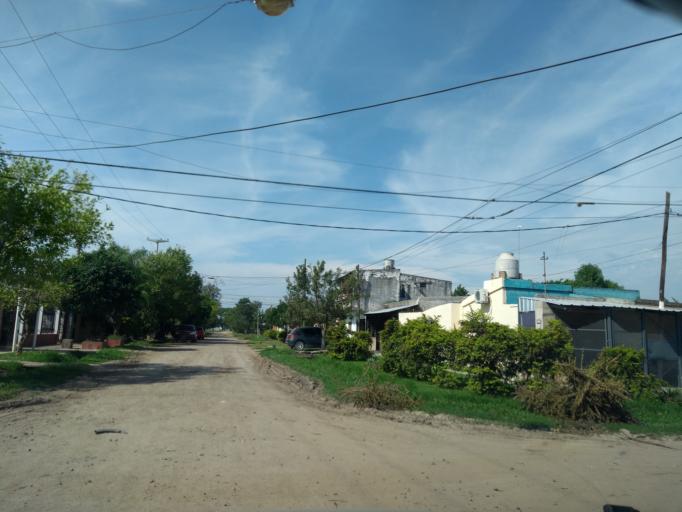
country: AR
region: Chaco
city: Resistencia
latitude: -27.4782
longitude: -58.9630
